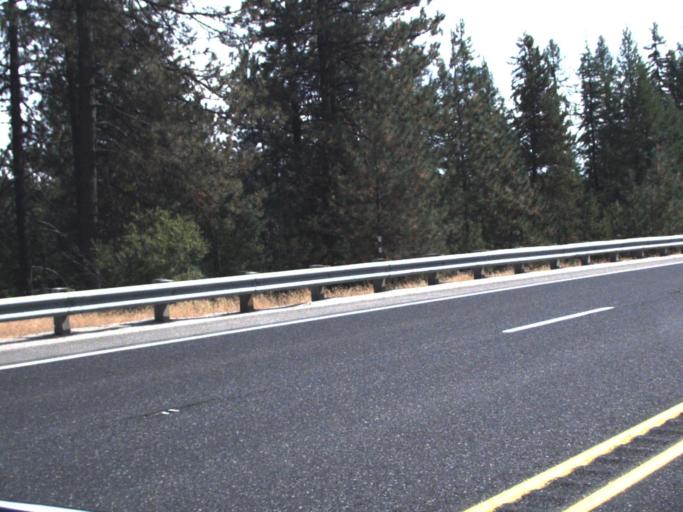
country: US
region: Washington
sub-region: Spokane County
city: Deer Park
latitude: 48.0244
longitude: -117.5933
